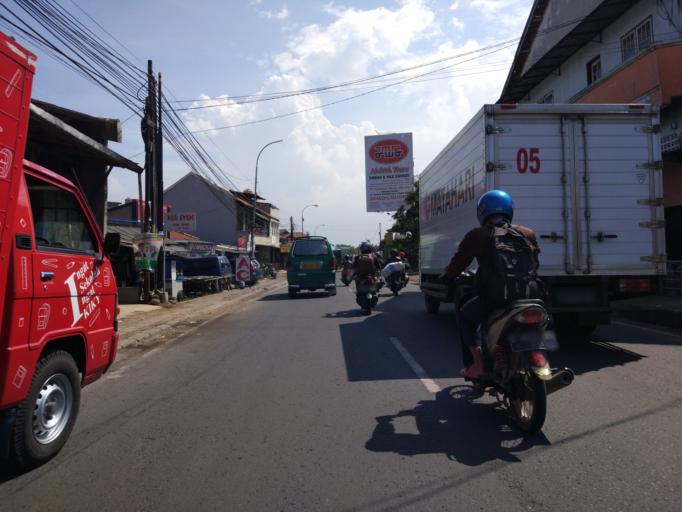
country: ID
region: West Java
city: Cileunyi
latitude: -6.9402
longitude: 107.7491
